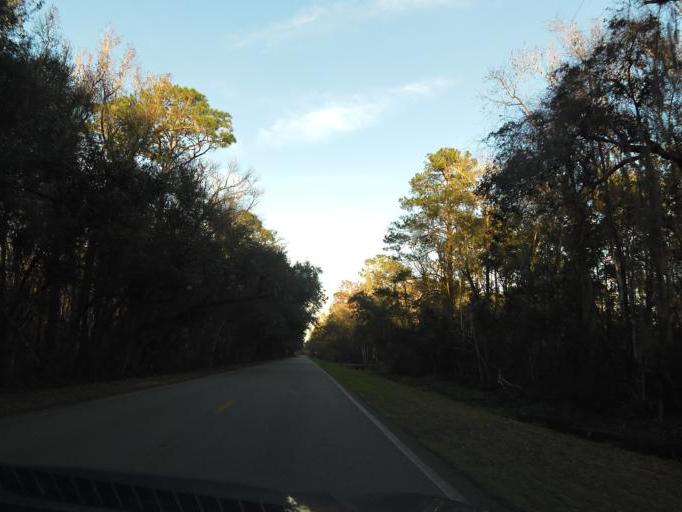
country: US
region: Florida
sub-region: Clay County
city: Green Cove Springs
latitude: 29.8591
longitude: -81.5514
